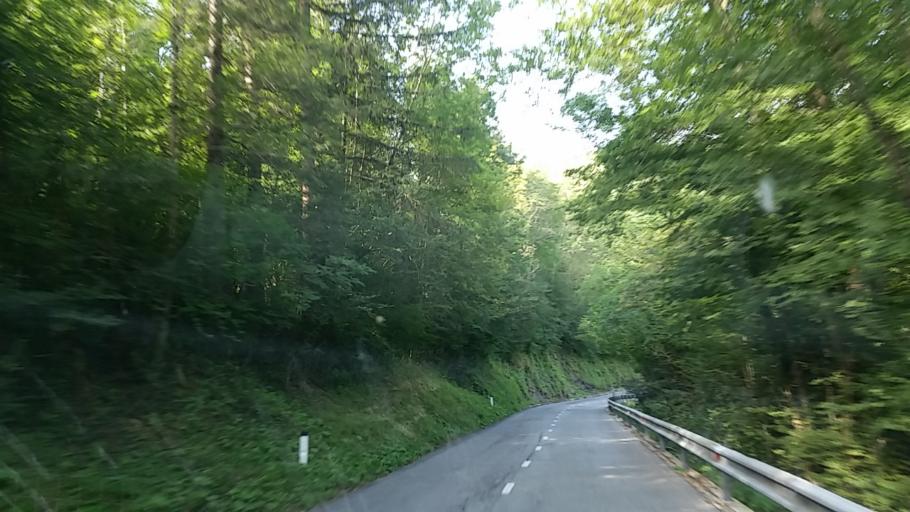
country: SI
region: Bovec
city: Bovec
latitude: 46.3403
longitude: 13.5744
